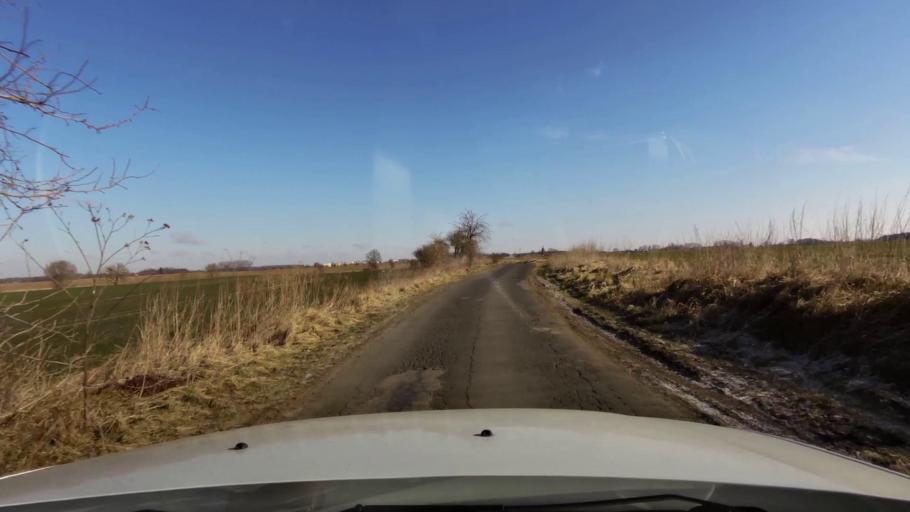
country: PL
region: West Pomeranian Voivodeship
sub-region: Powiat pyrzycki
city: Lipiany
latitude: 52.9841
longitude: 15.0387
